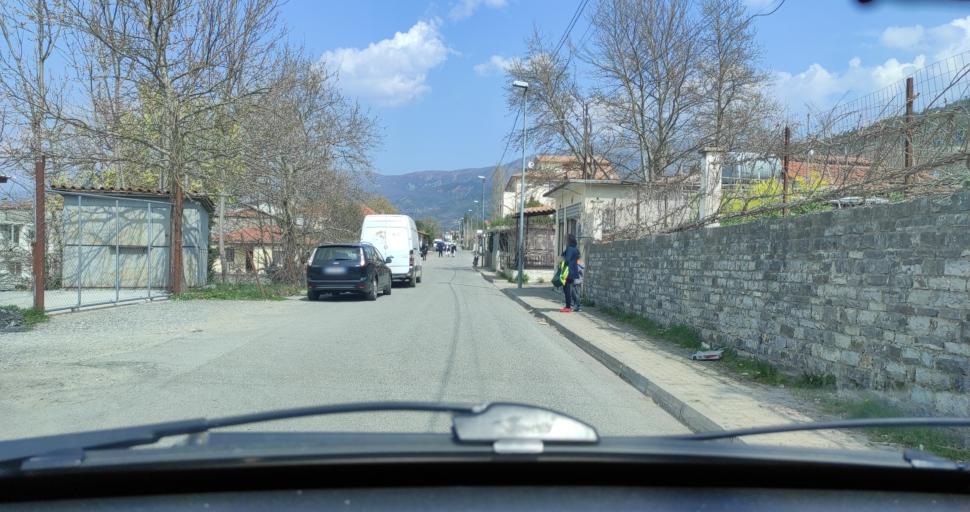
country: AL
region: Lezhe
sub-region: Rrethi i Lezhes
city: Kallmeti i Madh
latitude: 41.8484
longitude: 19.6900
